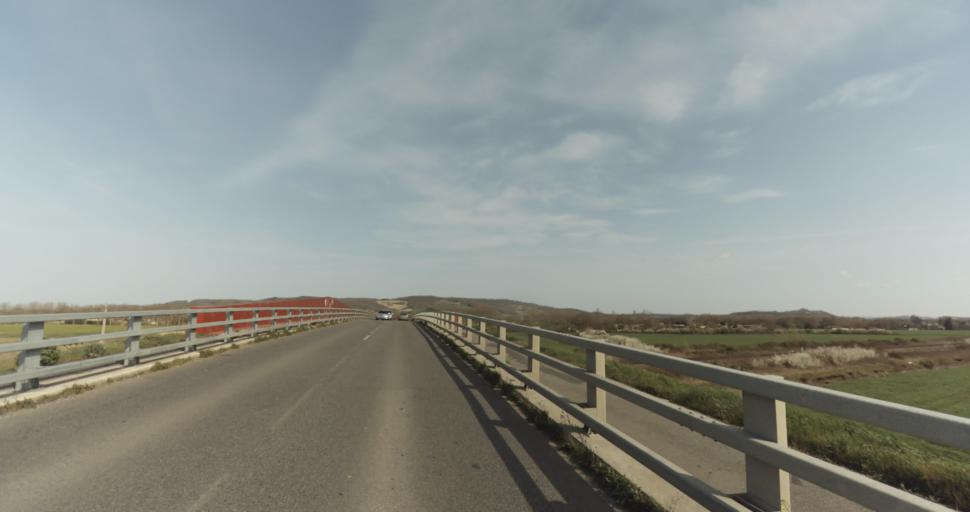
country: FR
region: Midi-Pyrenees
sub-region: Departement de la Haute-Garonne
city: Buzet-sur-Tarn
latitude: 43.7651
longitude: 1.6570
